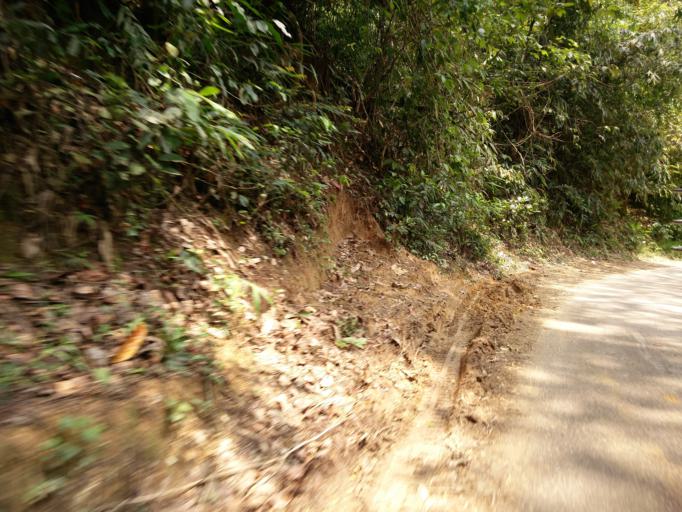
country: IN
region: Tripura
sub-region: Dhalai
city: Kamalpur
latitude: 24.3060
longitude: 91.7775
